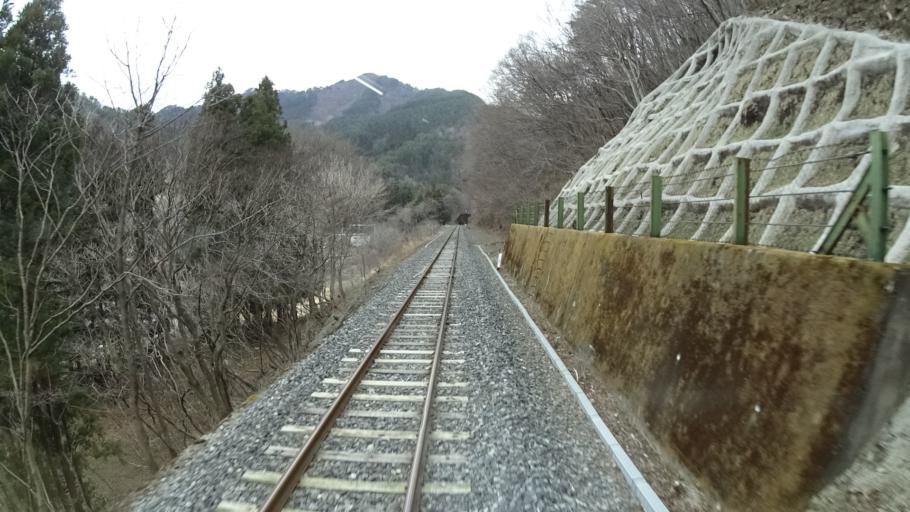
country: JP
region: Iwate
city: Kamaishi
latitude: 39.2919
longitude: 141.8630
